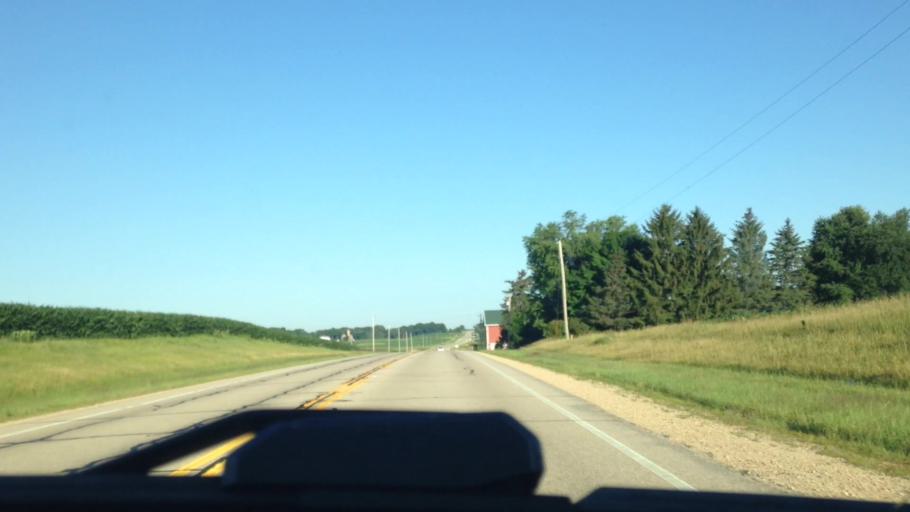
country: US
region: Wisconsin
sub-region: Columbia County
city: Fall River
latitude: 43.3403
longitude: -89.1595
